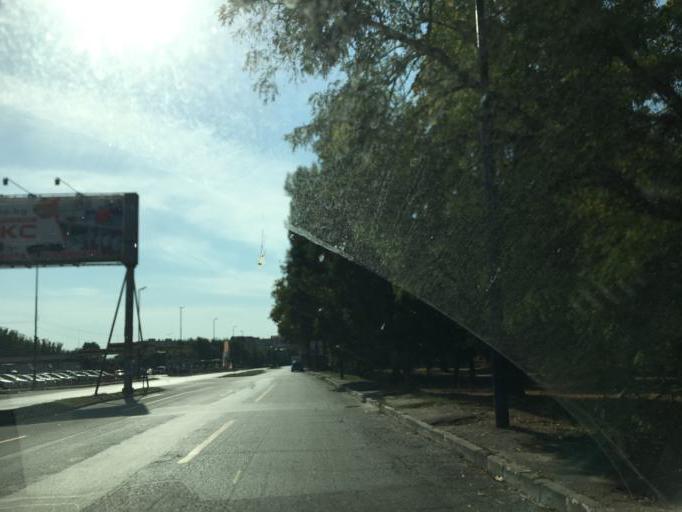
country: BG
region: Pazardzhik
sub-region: Obshtina Pazardzhik
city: Pazardzhik
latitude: 42.2089
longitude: 24.3260
